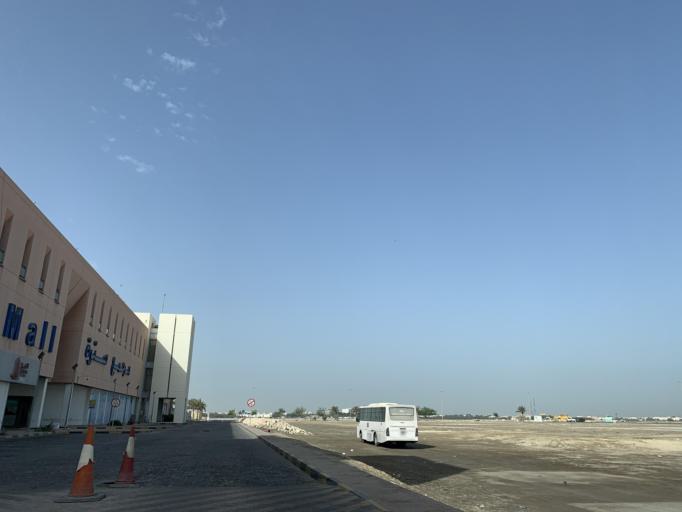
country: BH
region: Northern
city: Sitrah
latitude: 26.1700
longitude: 50.6009
